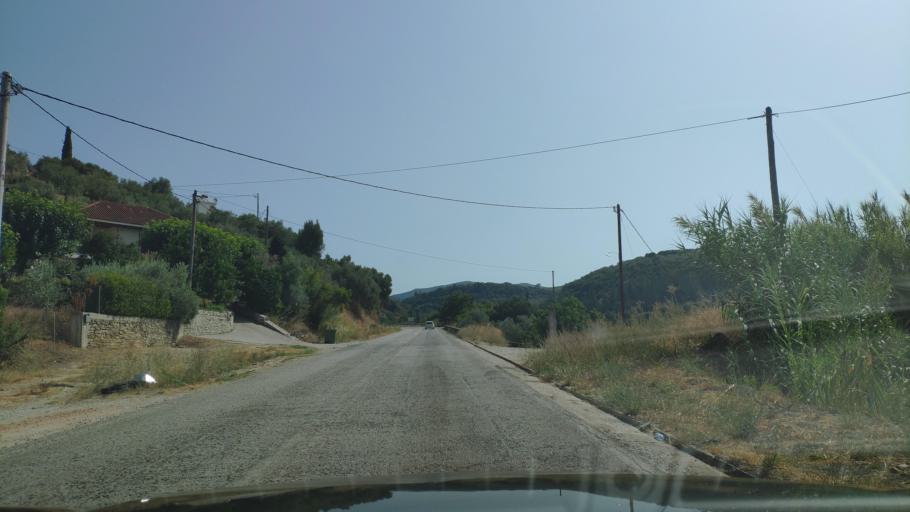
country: GR
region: Epirus
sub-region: Nomos Artas
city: Peta
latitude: 39.1581
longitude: 21.0300
